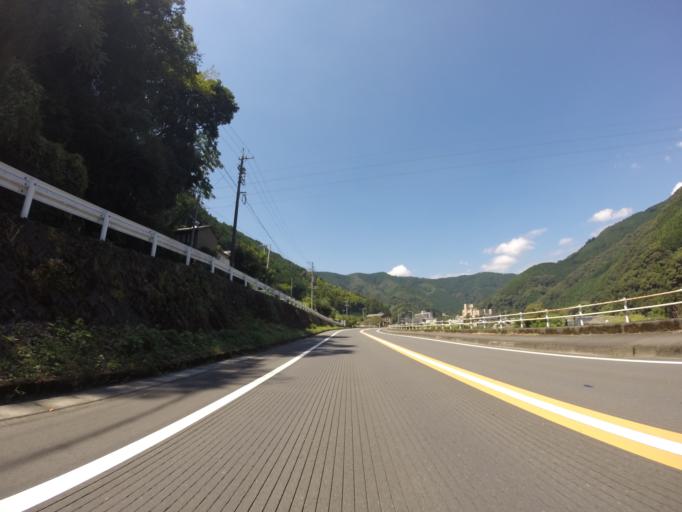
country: JP
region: Shizuoka
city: Shizuoka-shi
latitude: 35.0181
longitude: 138.2655
